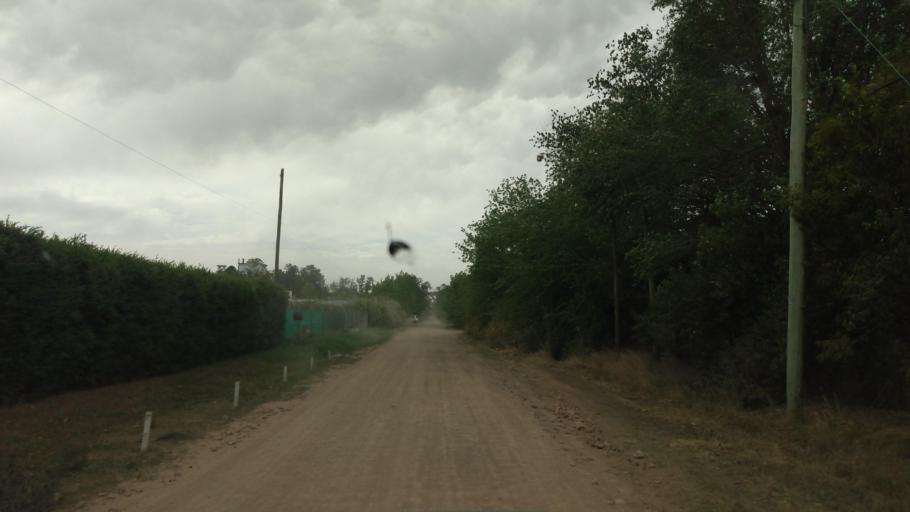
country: AR
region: Buenos Aires
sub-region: Partido de Lujan
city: Lujan
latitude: -34.5948
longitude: -59.1408
